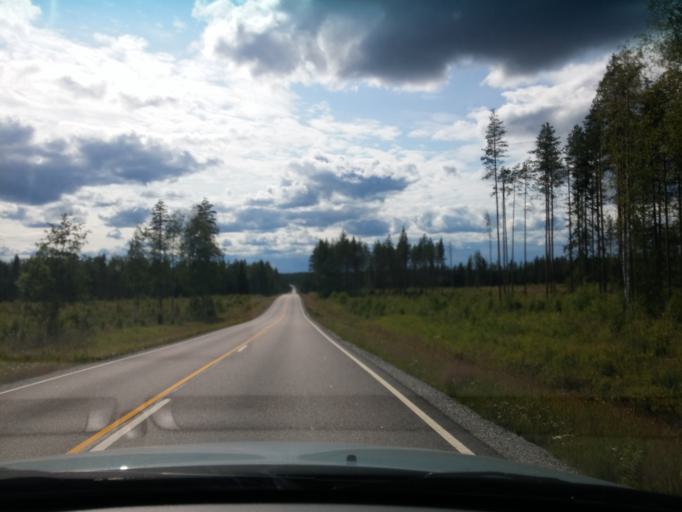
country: FI
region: Central Finland
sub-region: Saarijaervi-Viitasaari
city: Pylkoenmaeki
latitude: 62.5988
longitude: 24.6295
